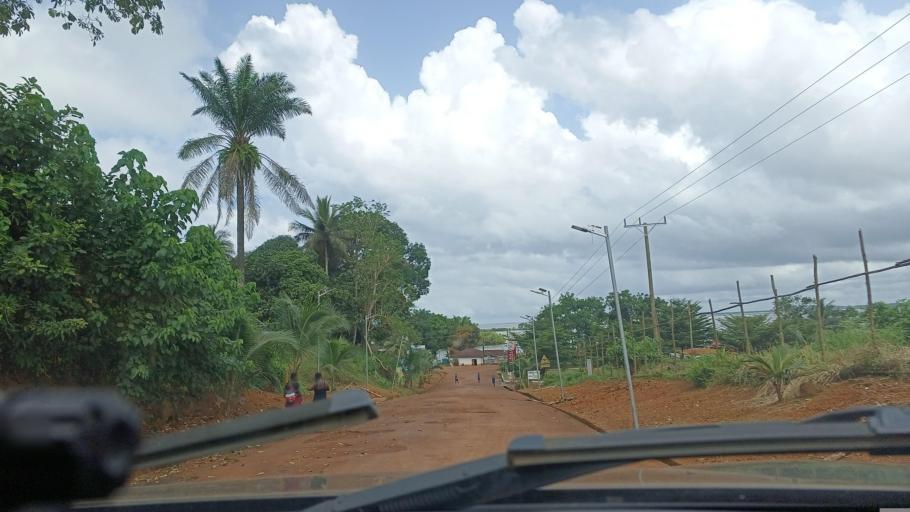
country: LR
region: Grand Cape Mount
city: Robertsport
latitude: 6.7529
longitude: -11.3634
